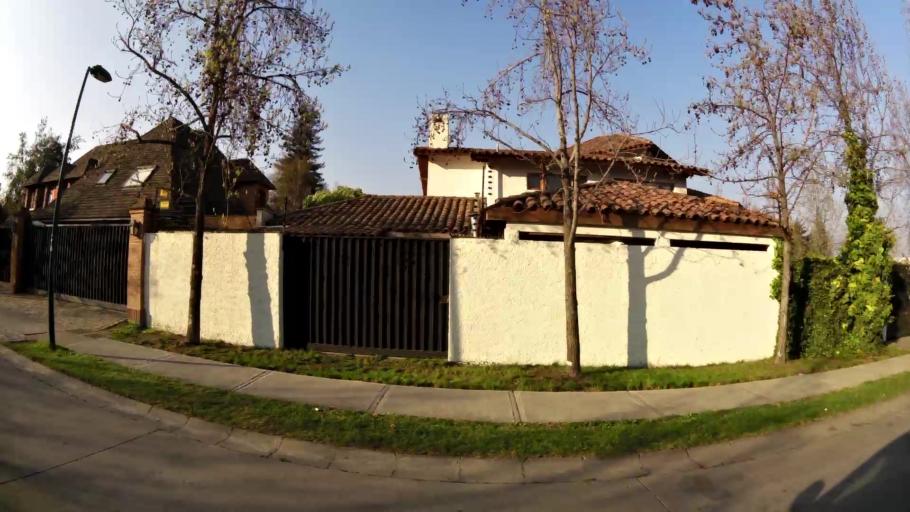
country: CL
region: Santiago Metropolitan
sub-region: Provincia de Santiago
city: Villa Presidente Frei, Nunoa, Santiago, Chile
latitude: -33.3571
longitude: -70.5437
